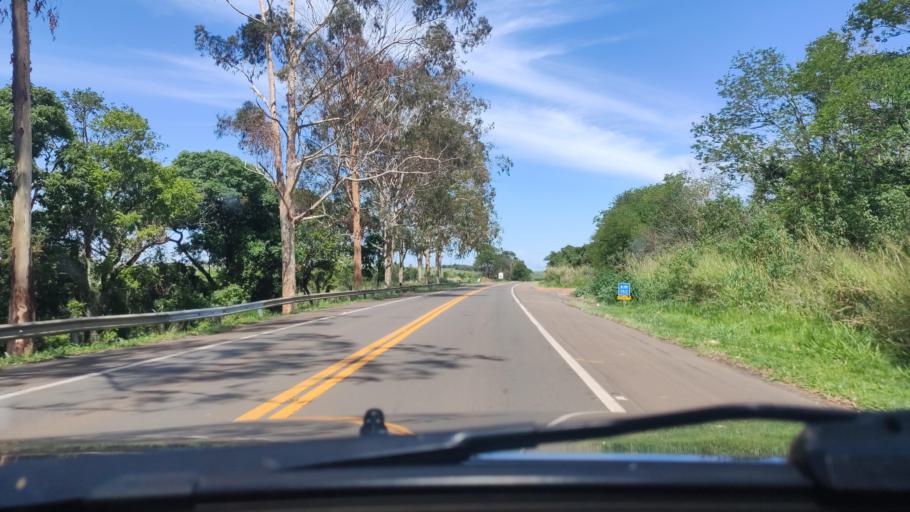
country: BR
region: Sao Paulo
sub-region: Sao Carlos
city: Sao Carlos
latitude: -22.0671
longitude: -47.9035
